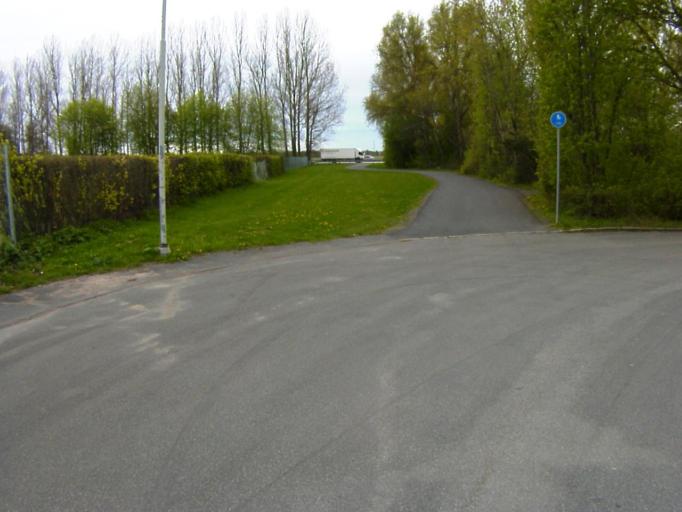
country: SE
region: Skane
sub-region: Kristianstads Kommun
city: Kristianstad
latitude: 56.0178
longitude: 14.1358
